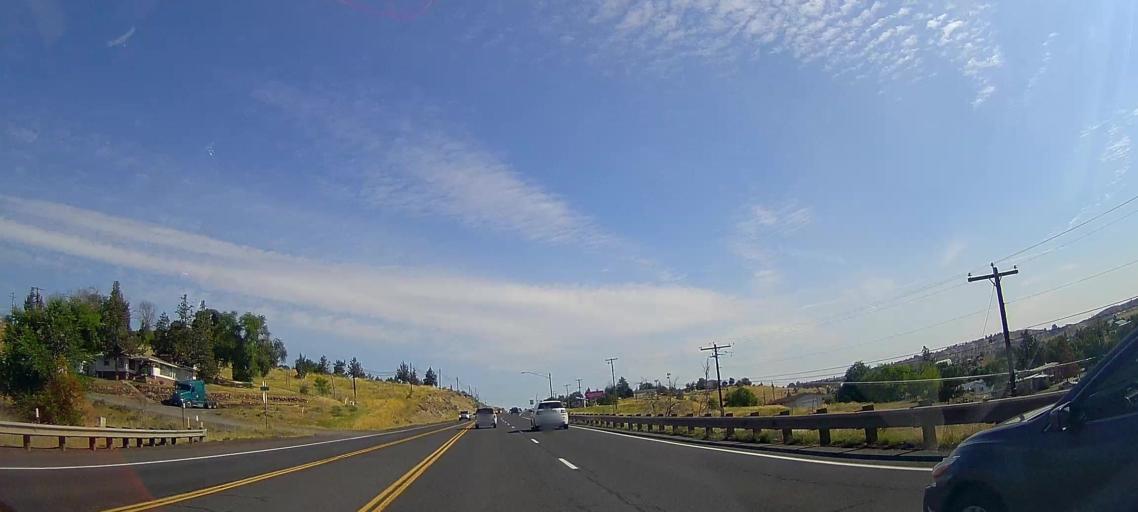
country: US
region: Oregon
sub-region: Jefferson County
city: Madras
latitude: 44.6464
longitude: -121.1294
